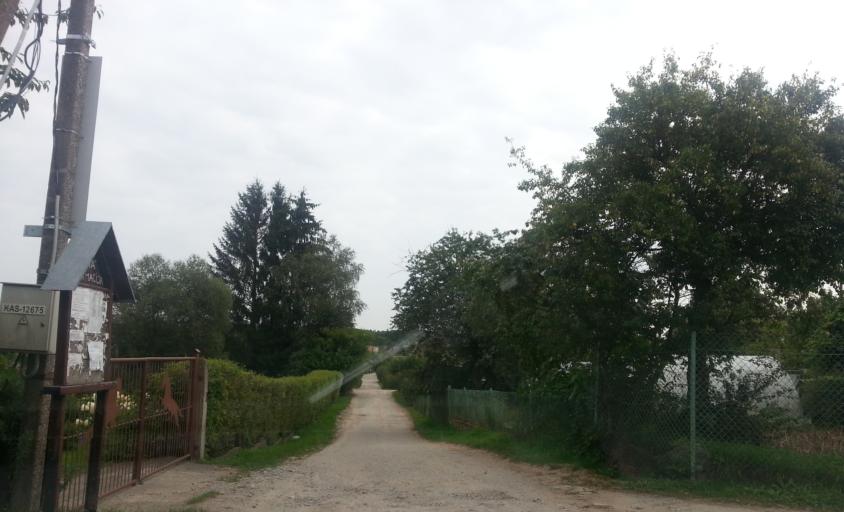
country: LT
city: Grigiskes
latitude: 54.7561
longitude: 25.0143
